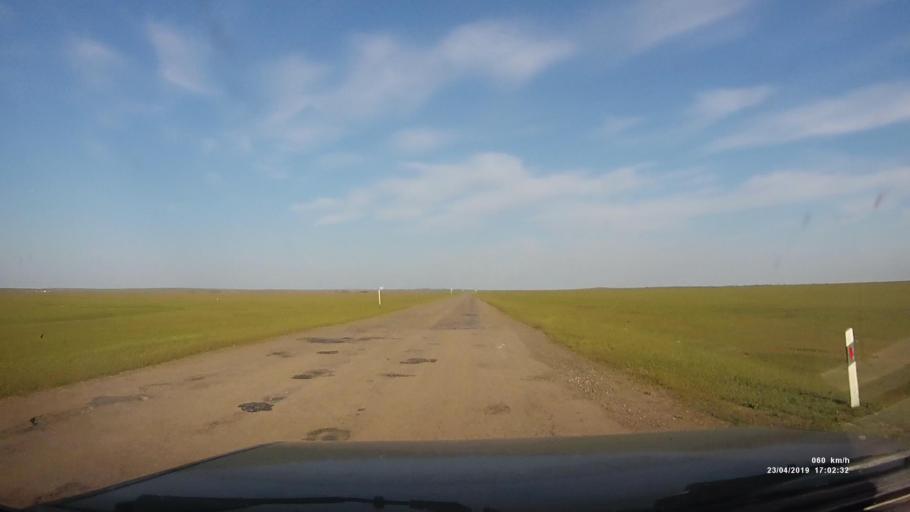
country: RU
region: Kalmykiya
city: Priyutnoye
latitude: 46.2924
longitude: 43.4189
